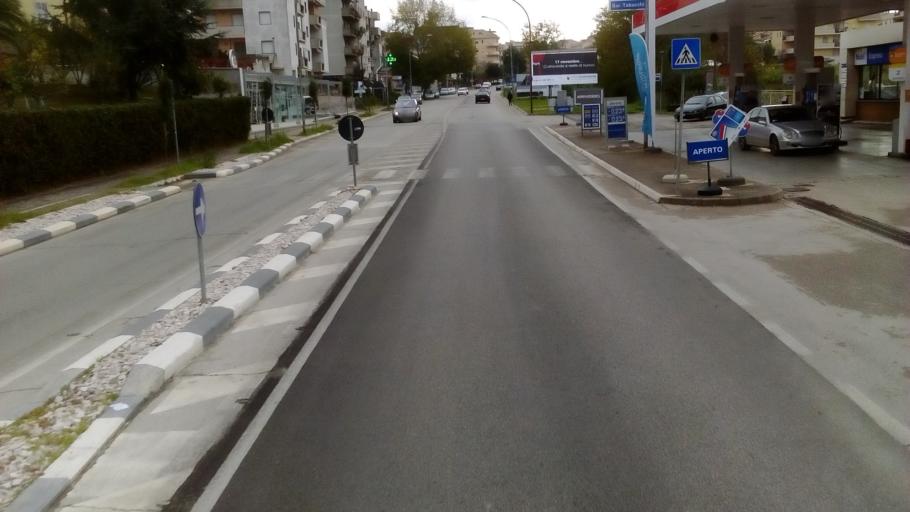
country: IT
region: Abruzzo
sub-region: Provincia di Chieti
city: Vasto
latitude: 42.1109
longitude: 14.7011
